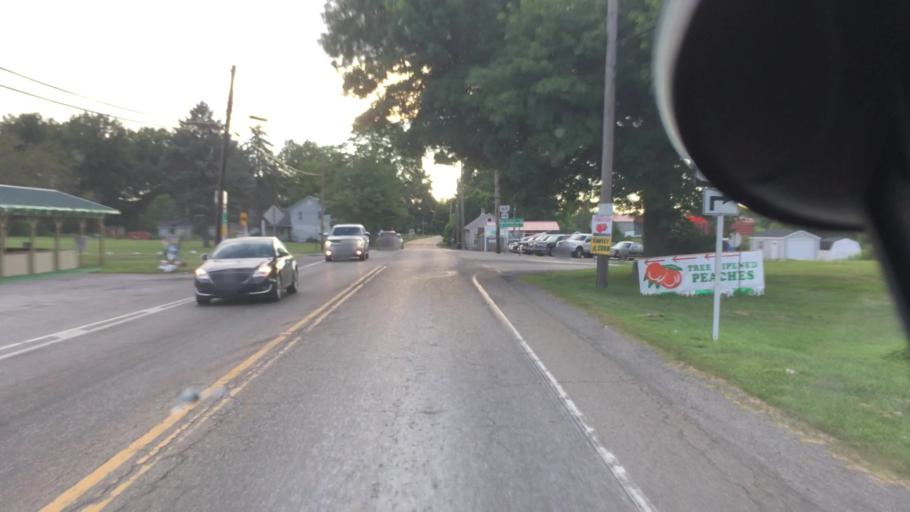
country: US
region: Ohio
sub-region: Columbiana County
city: East Palestine
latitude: 40.8651
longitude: -80.5590
